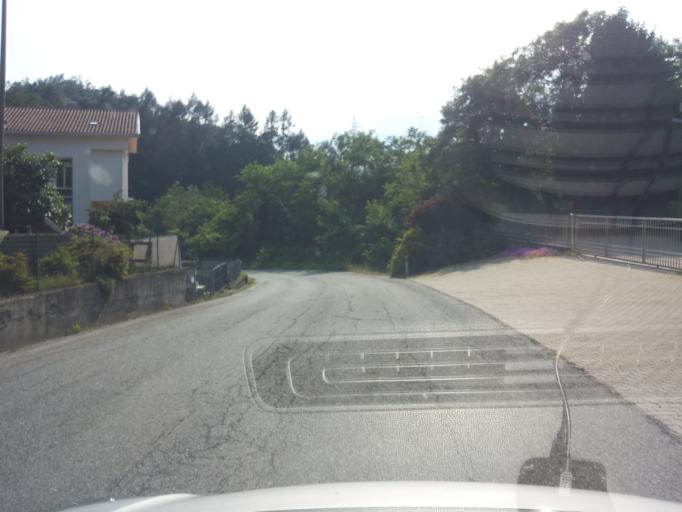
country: IT
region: Piedmont
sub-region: Provincia di Biella
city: Lanvario
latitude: 45.6530
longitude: 8.1997
